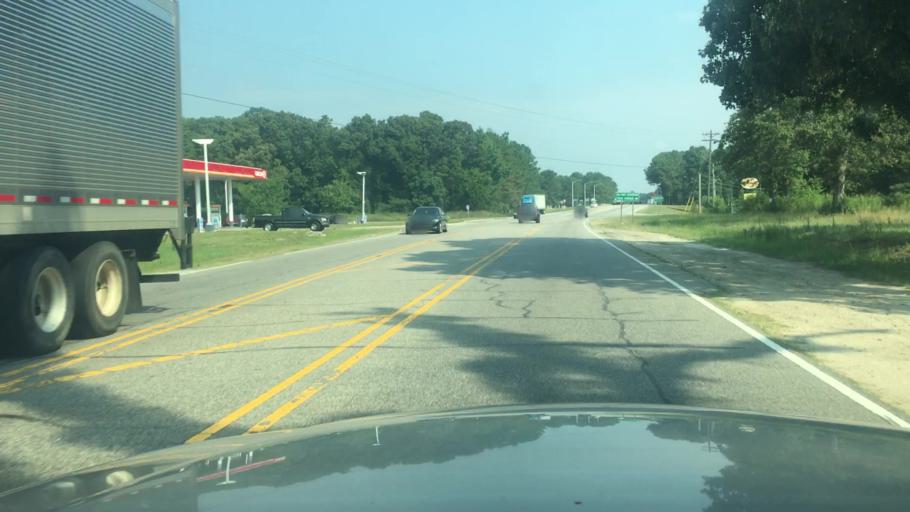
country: US
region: North Carolina
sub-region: Cumberland County
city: Hope Mills
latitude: 34.9349
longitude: -78.9203
